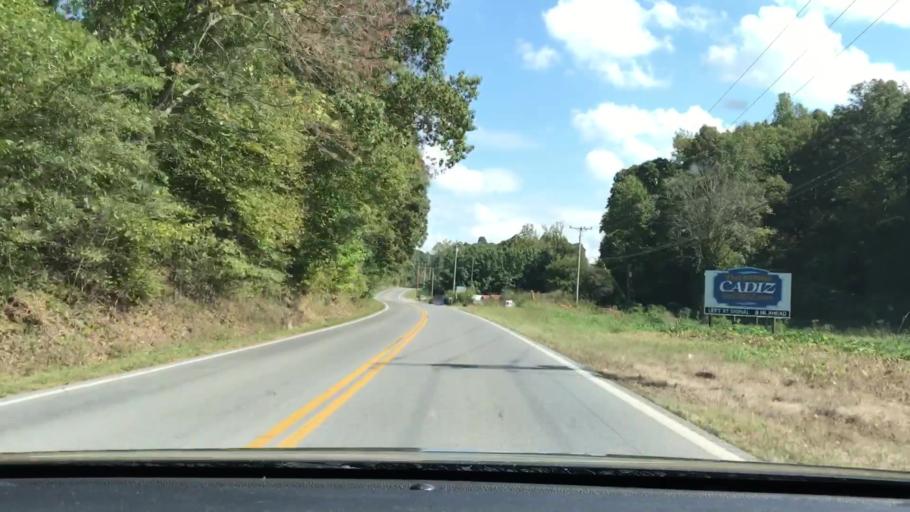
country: US
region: Kentucky
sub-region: Trigg County
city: Cadiz
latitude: 36.8073
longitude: -87.9062
